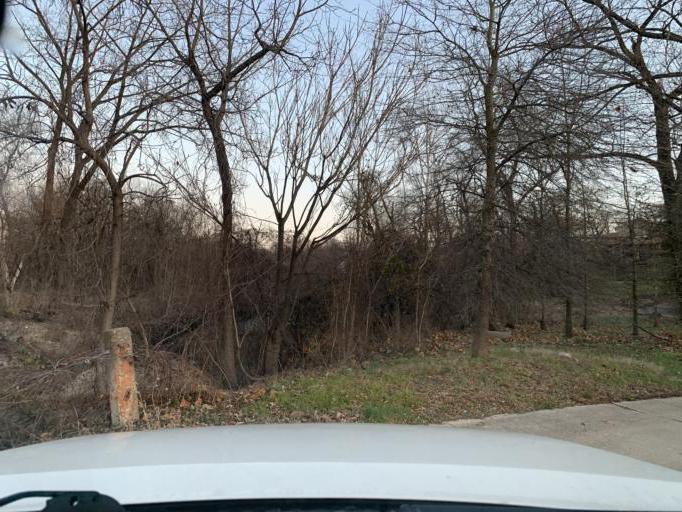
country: US
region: Maryland
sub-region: Prince George's County
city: Fairmount Heights
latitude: 38.8983
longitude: -76.9360
